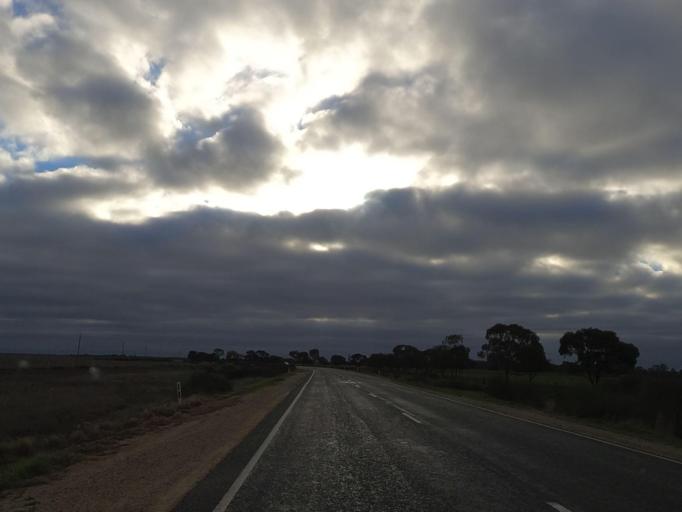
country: AU
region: Victoria
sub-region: Swan Hill
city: Swan Hill
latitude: -35.6523
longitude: 143.8458
